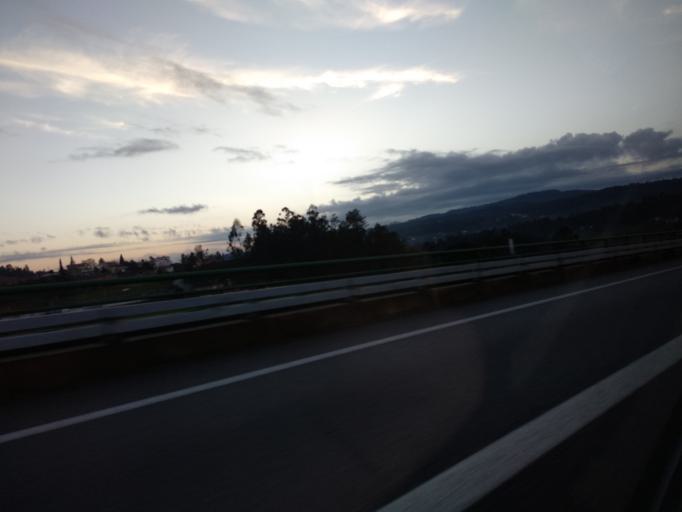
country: PT
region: Braga
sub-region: Braga
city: Oliveira
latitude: 41.4977
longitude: -8.4711
